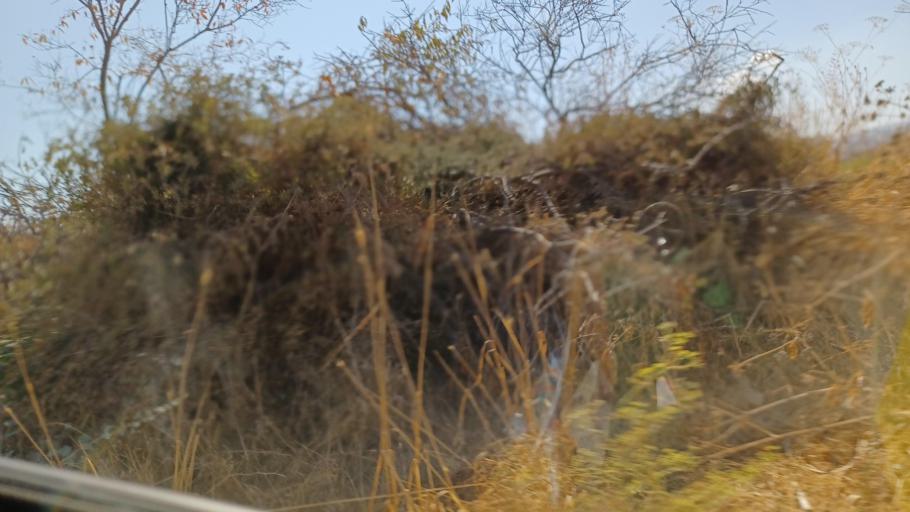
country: CY
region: Pafos
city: Polis
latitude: 35.0030
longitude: 32.4462
